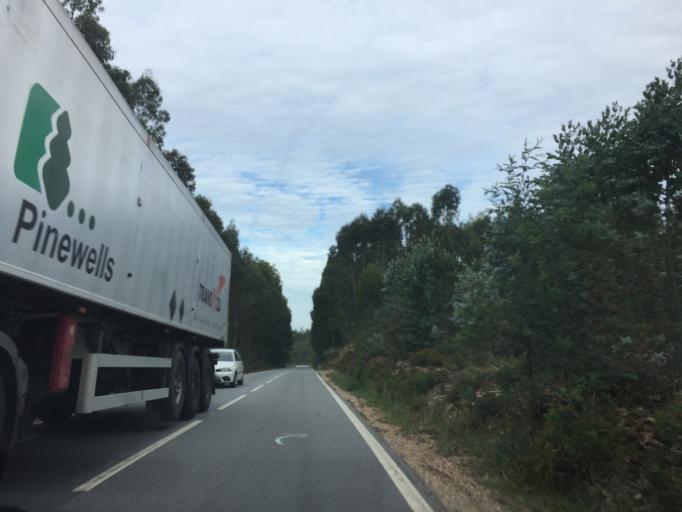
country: PT
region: Aveiro
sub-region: Agueda
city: Aguada de Cima
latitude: 40.4929
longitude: -8.3387
